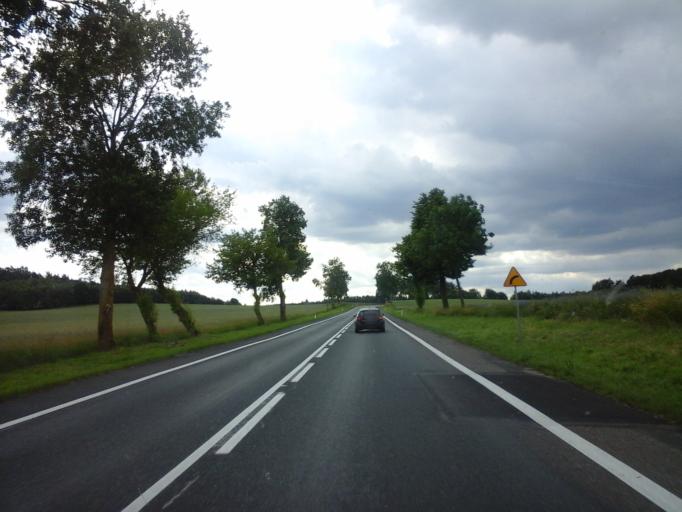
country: PL
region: West Pomeranian Voivodeship
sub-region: Powiat bialogardzki
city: Karlino
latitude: 54.0017
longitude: 15.7798
